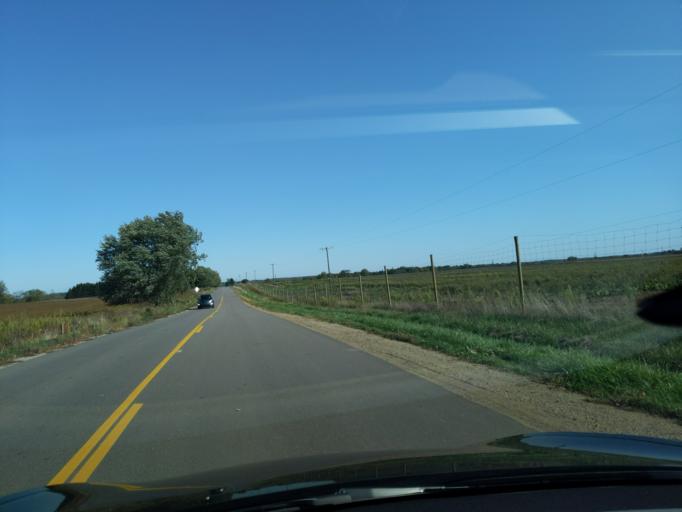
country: US
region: Michigan
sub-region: Eaton County
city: Potterville
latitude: 42.6404
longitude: -84.7974
